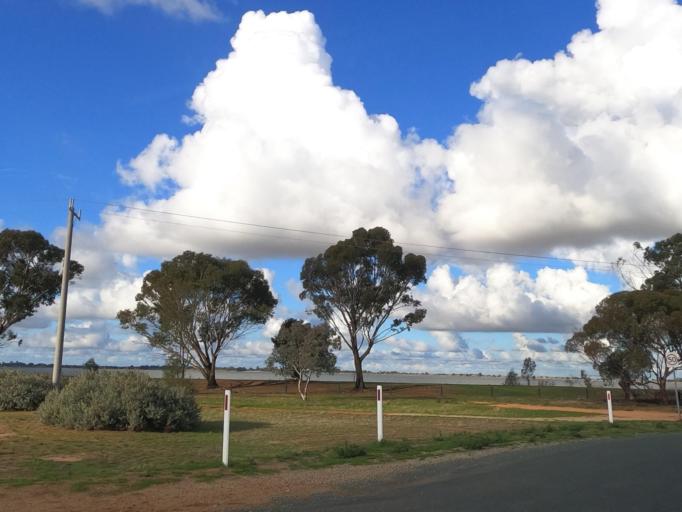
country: AU
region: Victoria
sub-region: Swan Hill
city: Swan Hill
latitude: -35.4478
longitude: 143.6269
